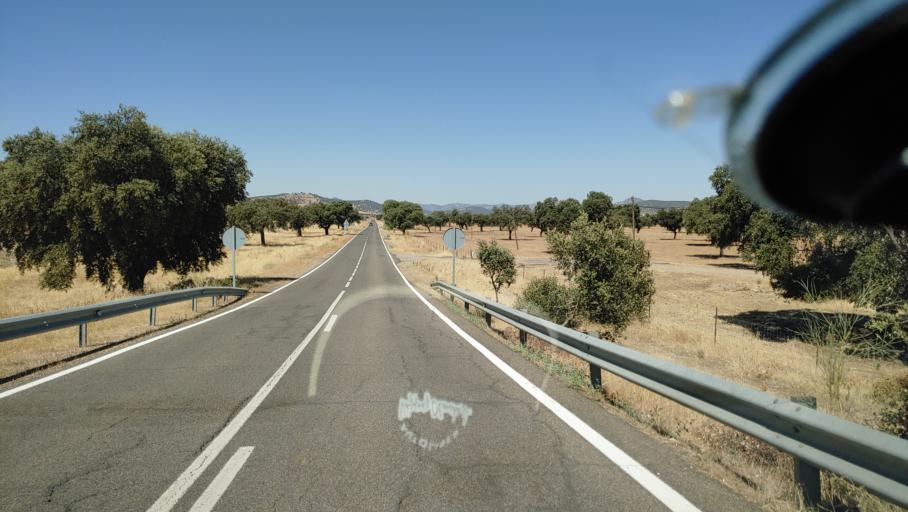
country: ES
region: Castille-La Mancha
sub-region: Provincia de Ciudad Real
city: Guadalmez
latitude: 38.7044
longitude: -4.9461
